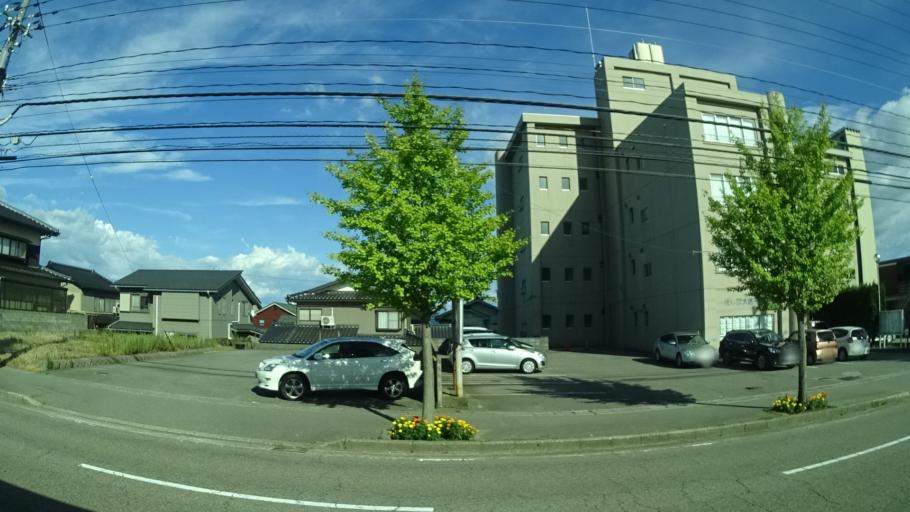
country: JP
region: Ishikawa
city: Kanazawa-shi
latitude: 36.6534
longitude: 136.6461
